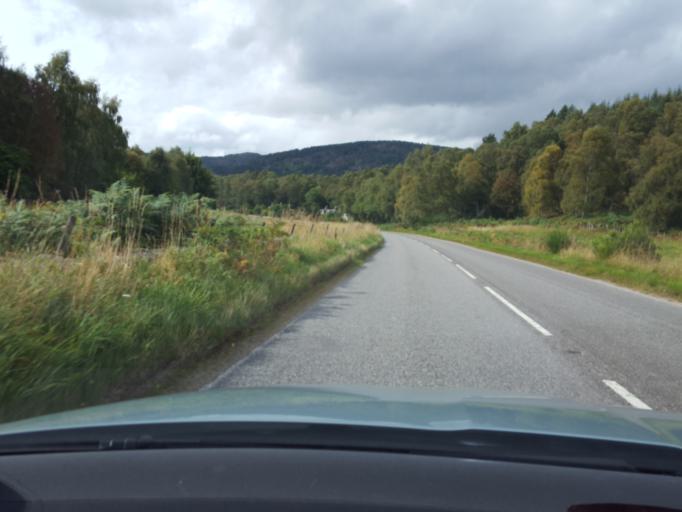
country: GB
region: Scotland
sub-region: Aberdeenshire
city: Ballater
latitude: 57.0704
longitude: -2.9656
